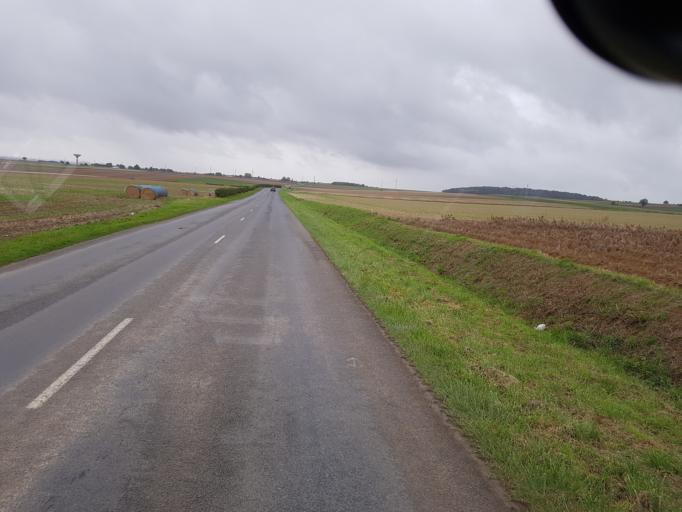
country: FR
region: Nord-Pas-de-Calais
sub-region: Departement du Pas-de-Calais
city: Neuville-Saint-Vaast
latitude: 50.3418
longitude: 2.7364
